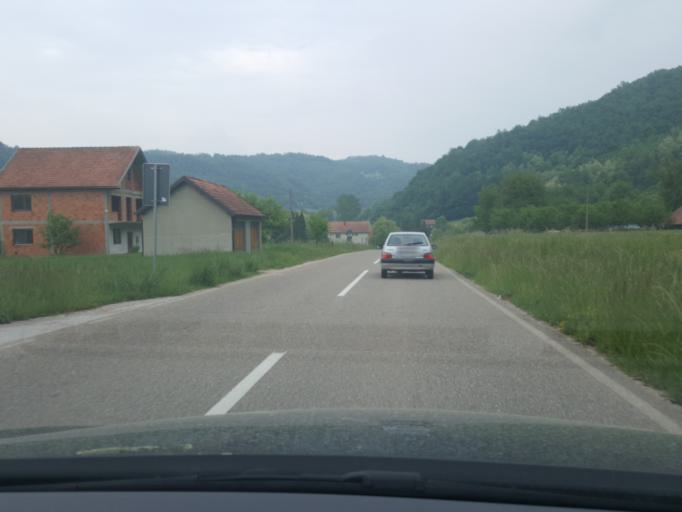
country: RS
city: Kamenica
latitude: 44.2472
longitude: 19.7647
